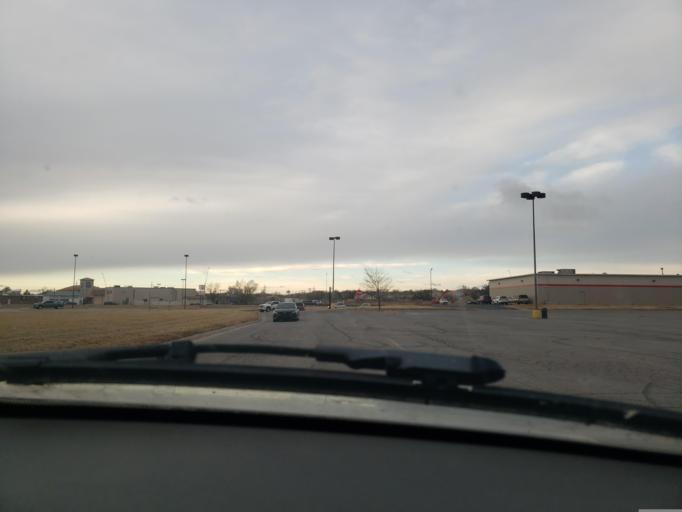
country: US
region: Kansas
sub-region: Finney County
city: Garden City
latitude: 37.9756
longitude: -100.8439
